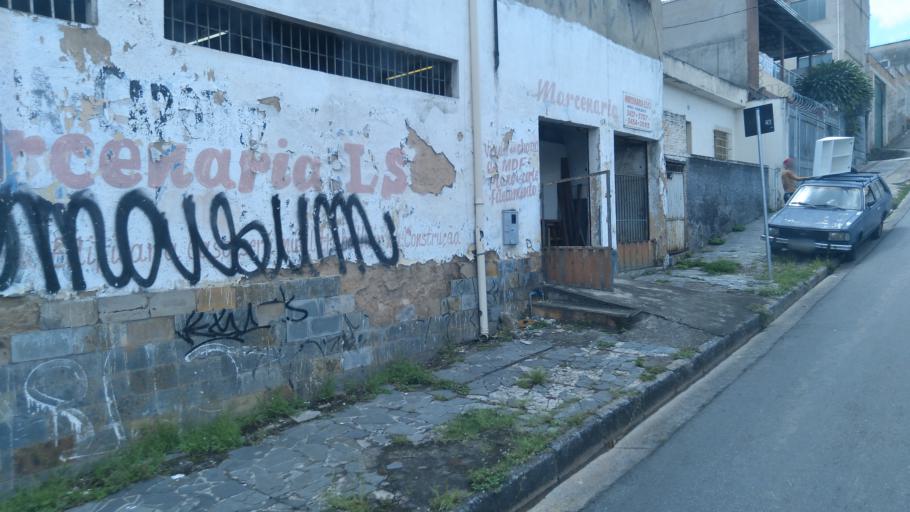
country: BR
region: Minas Gerais
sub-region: Belo Horizonte
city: Belo Horizonte
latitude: -19.8527
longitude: -43.8972
